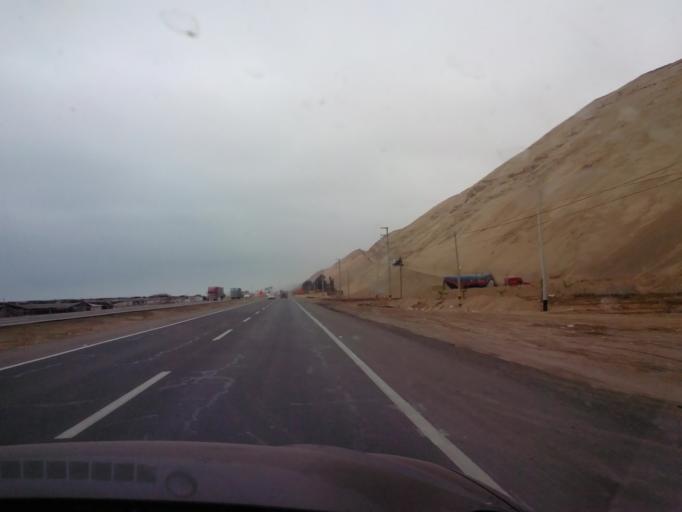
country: PE
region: Ica
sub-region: Provincia de Chincha
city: San Pedro
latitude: -13.3399
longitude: -76.2311
